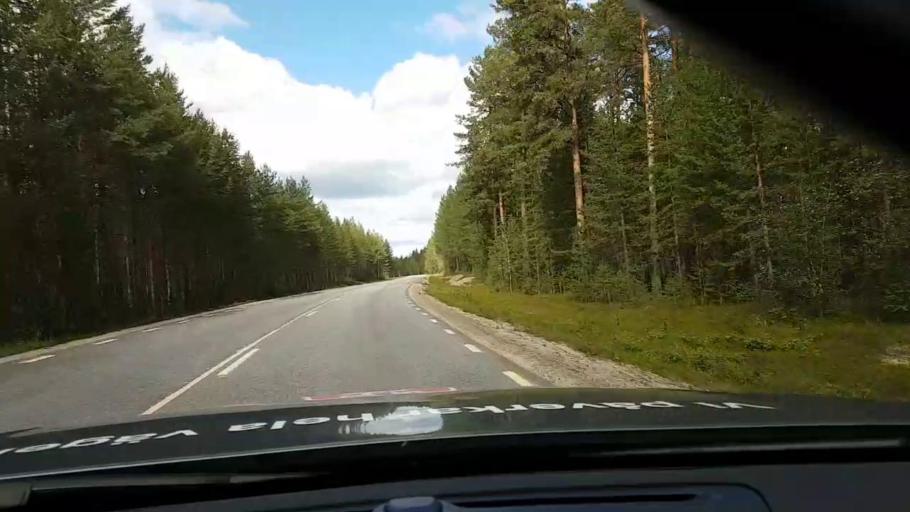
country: SE
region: Vaesternorrland
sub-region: OErnskoeldsviks Kommun
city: Bredbyn
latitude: 63.5328
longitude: 17.9672
